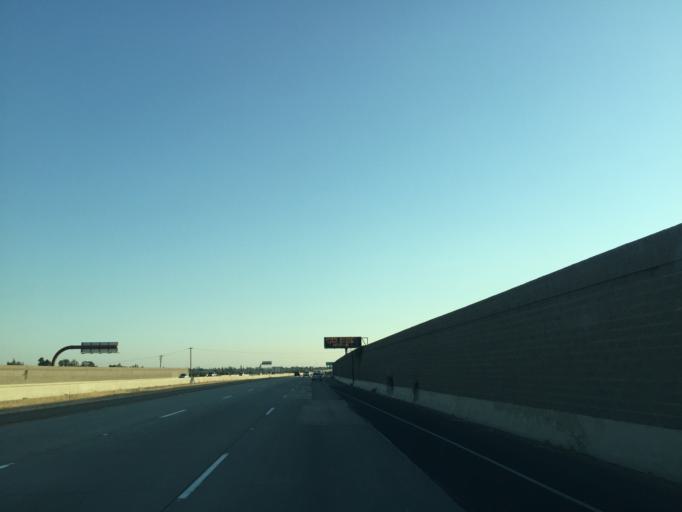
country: US
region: California
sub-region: Fresno County
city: Tarpey Village
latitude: 36.8038
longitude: -119.7380
